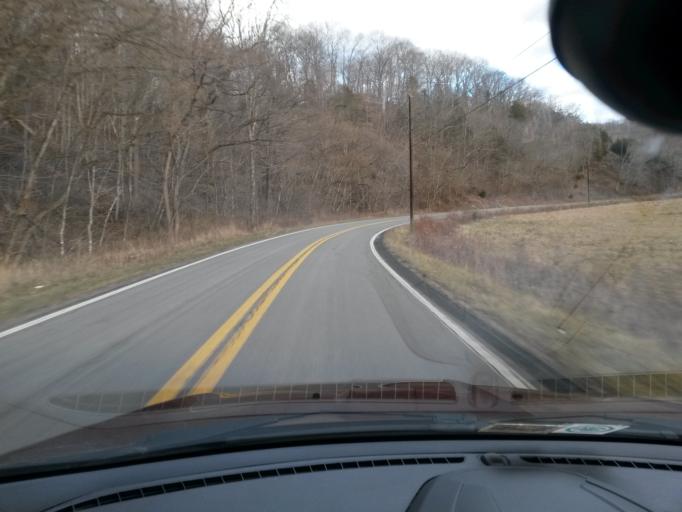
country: US
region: West Virginia
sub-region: Monroe County
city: Union
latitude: 37.5472
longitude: -80.5809
